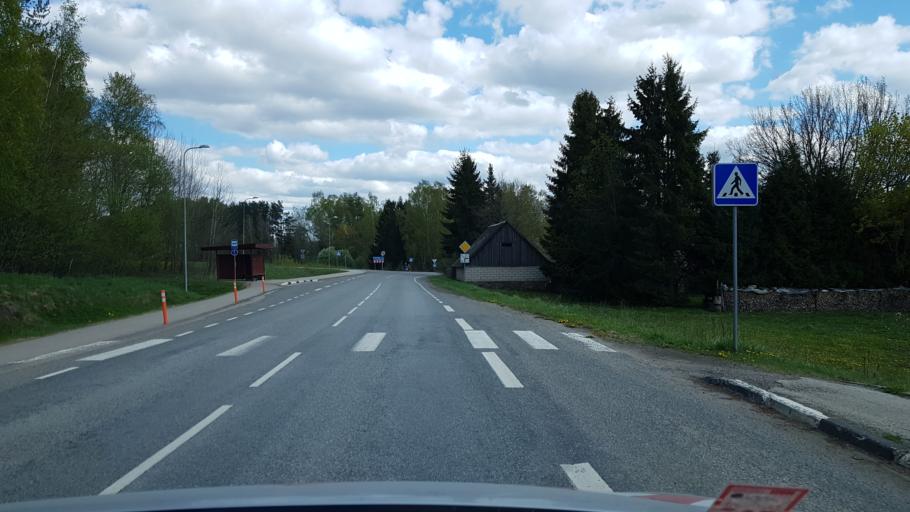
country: EE
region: Tartu
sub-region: UElenurme vald
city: Ulenurme
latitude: 58.2939
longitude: 26.8909
